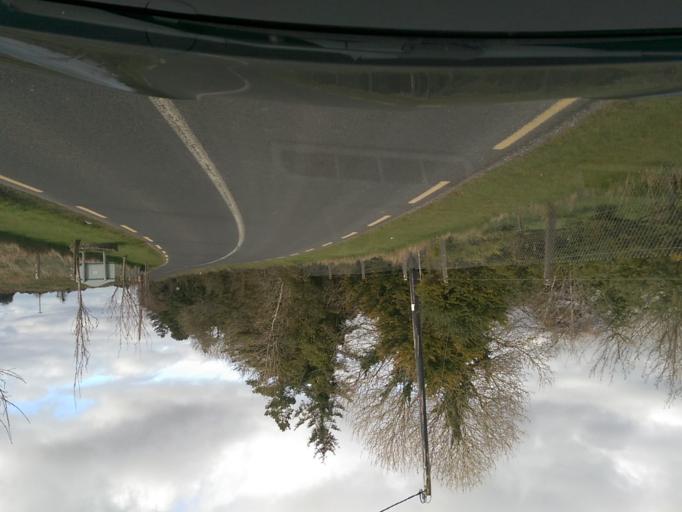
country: IE
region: Connaught
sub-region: County Galway
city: Ballinasloe
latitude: 53.3337
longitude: -8.3945
